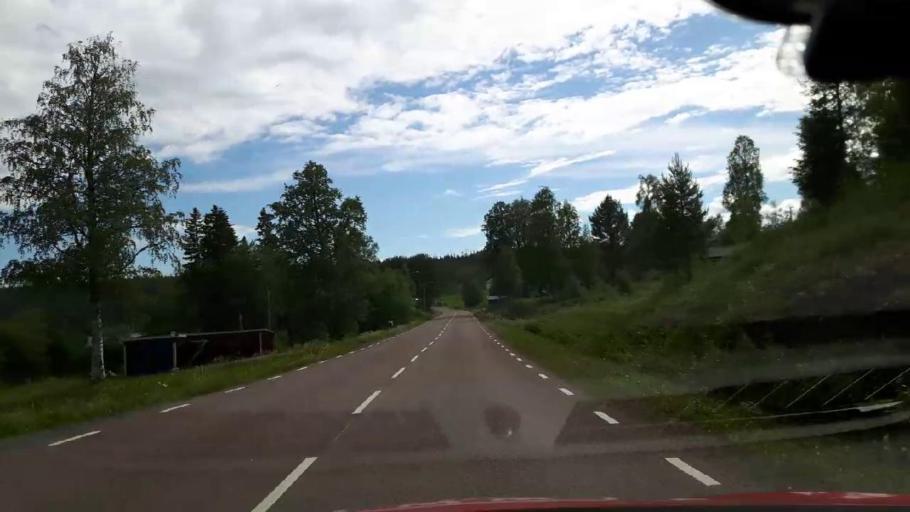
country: SE
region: Jaemtland
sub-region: Krokoms Kommun
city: Valla
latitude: 63.9098
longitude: 14.2157
